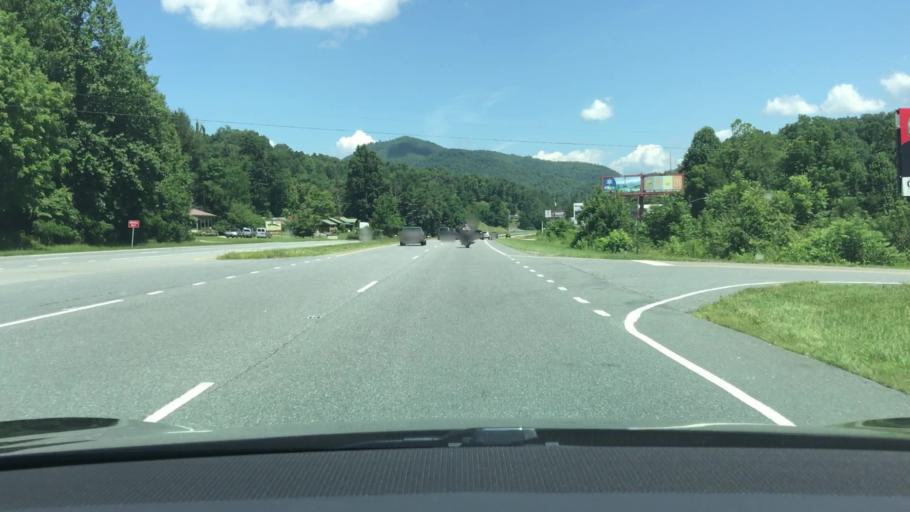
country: US
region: North Carolina
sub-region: Jackson County
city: Sylva
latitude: 35.3160
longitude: -83.2616
